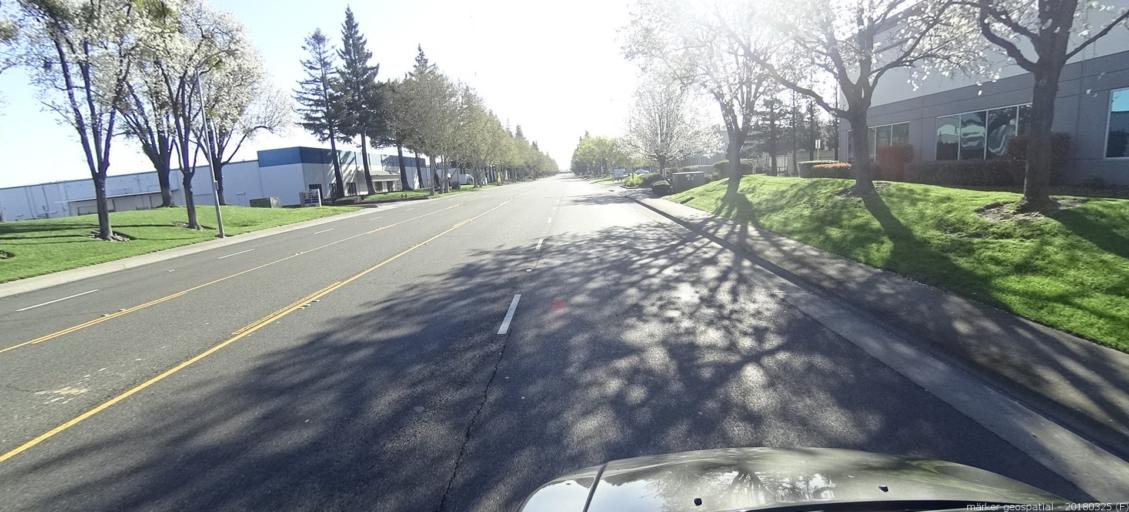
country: US
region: California
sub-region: Sacramento County
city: Rio Linda
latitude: 38.6472
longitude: -121.4845
